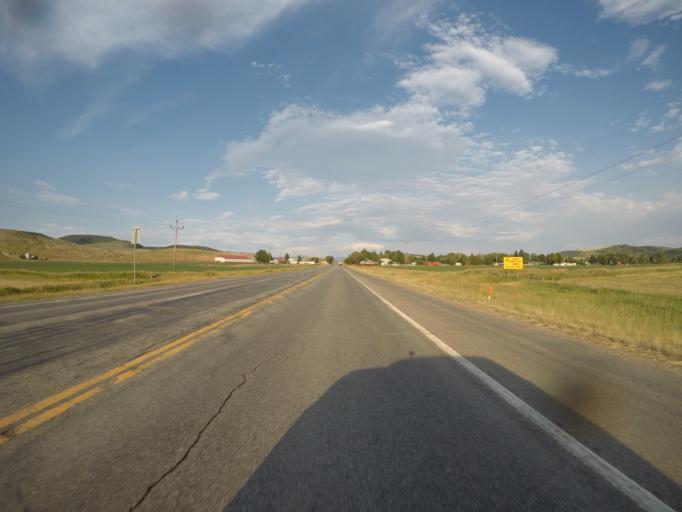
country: US
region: Colorado
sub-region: Routt County
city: Steamboat Springs
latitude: 40.4857
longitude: -107.0261
